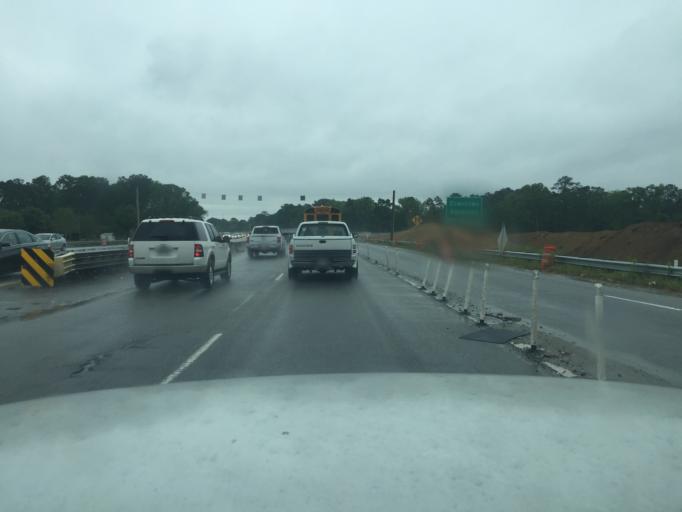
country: US
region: Georgia
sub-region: Chatham County
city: Georgetown
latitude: 31.9859
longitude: -81.2175
